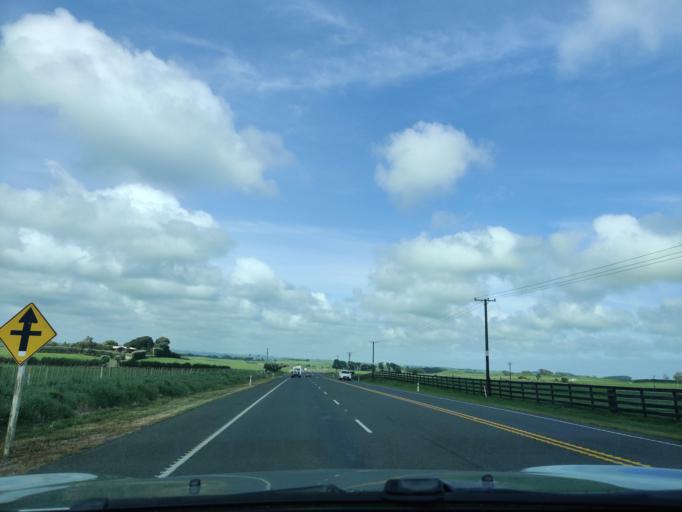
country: NZ
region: Taranaki
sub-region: South Taranaki District
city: Patea
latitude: -39.7659
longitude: 174.6494
